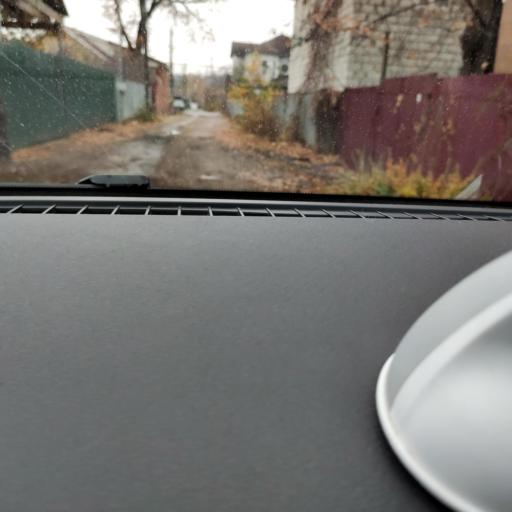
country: RU
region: Samara
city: Samara
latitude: 53.2737
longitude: 50.2105
